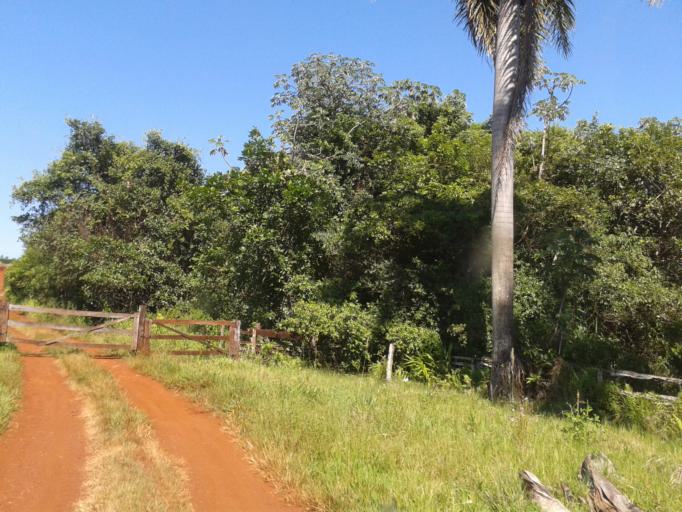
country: BR
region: Minas Gerais
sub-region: Centralina
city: Centralina
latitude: -18.6515
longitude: -49.2979
